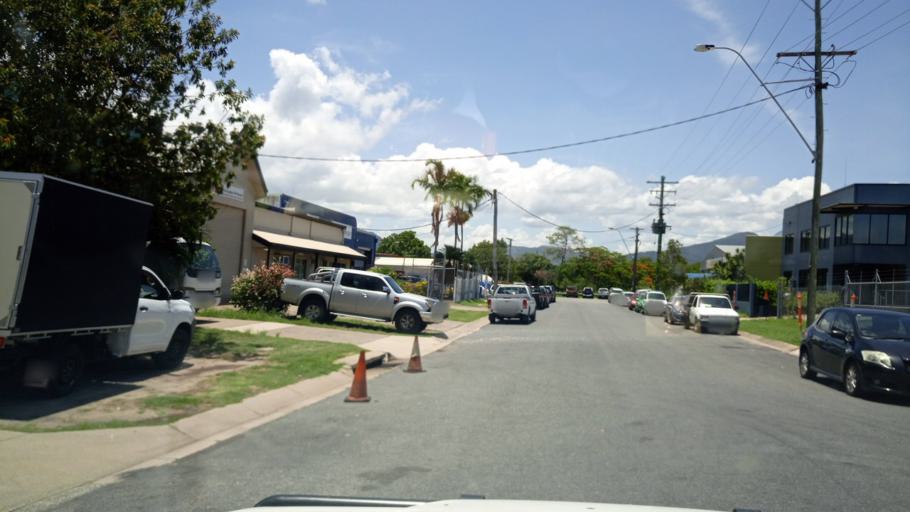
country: AU
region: Queensland
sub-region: Cairns
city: Redlynch
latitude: -16.8727
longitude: 145.7386
